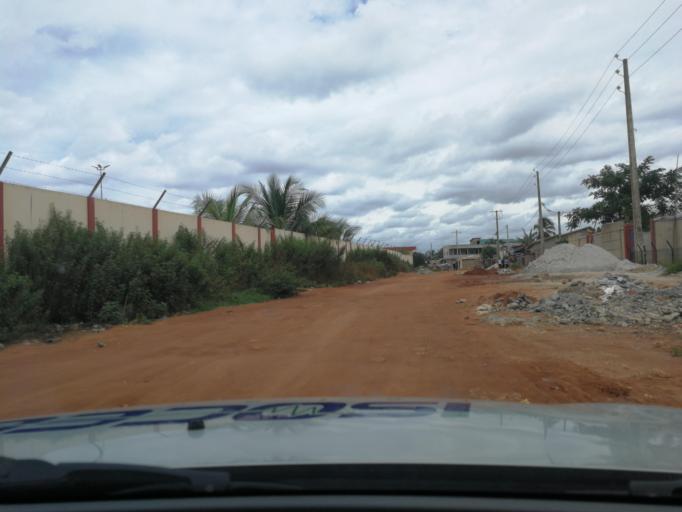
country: BJ
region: Atlantique
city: Abomey-Calavi
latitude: 6.4300
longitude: 2.3068
